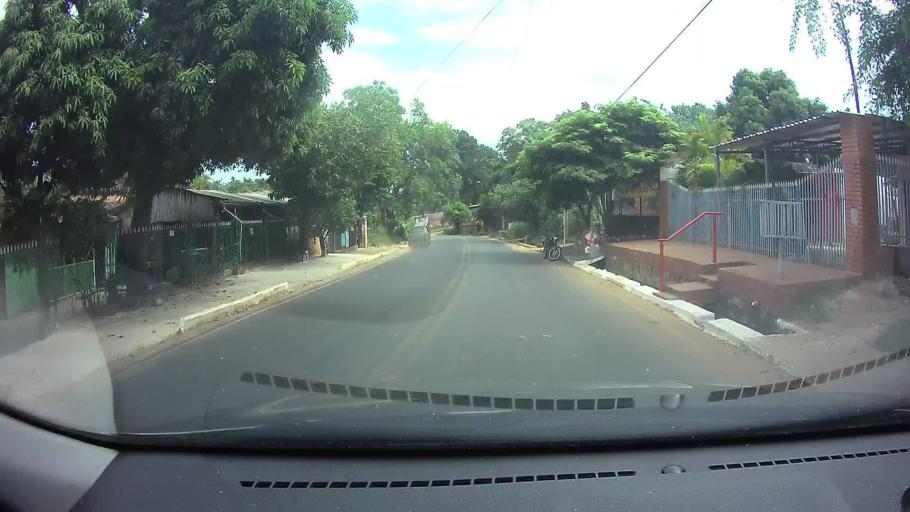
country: PY
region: Central
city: Fernando de la Mora
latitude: -25.2931
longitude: -57.5118
